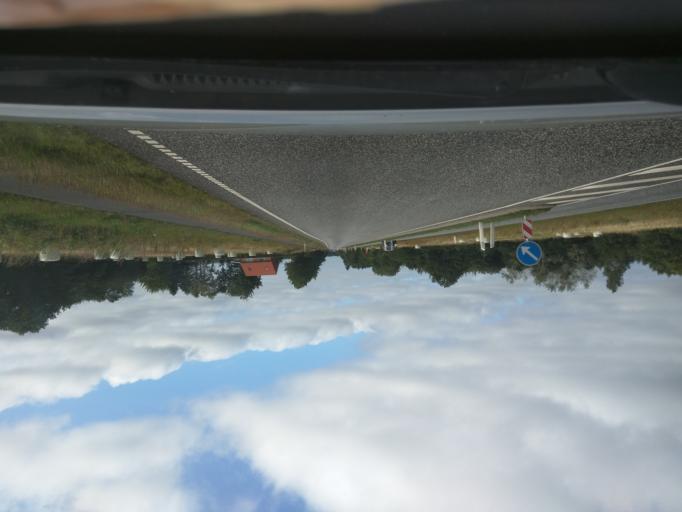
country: DK
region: Central Jutland
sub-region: Viborg Kommune
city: Viborg
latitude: 56.4116
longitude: 9.3756
